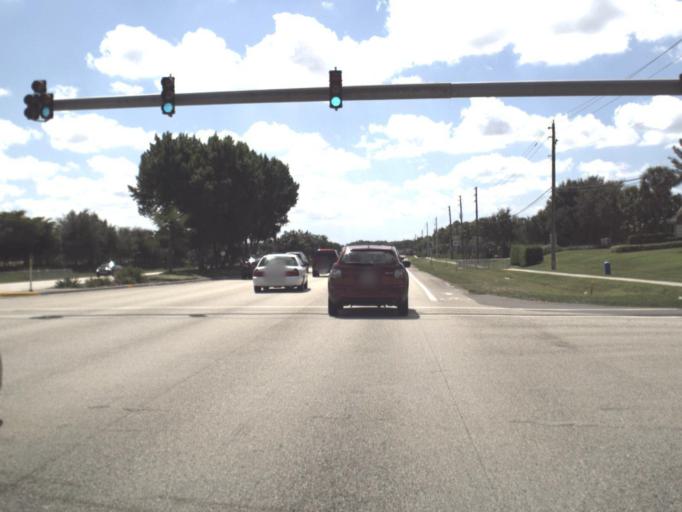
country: US
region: Florida
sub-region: Lee County
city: Estero
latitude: 26.4206
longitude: -81.8118
